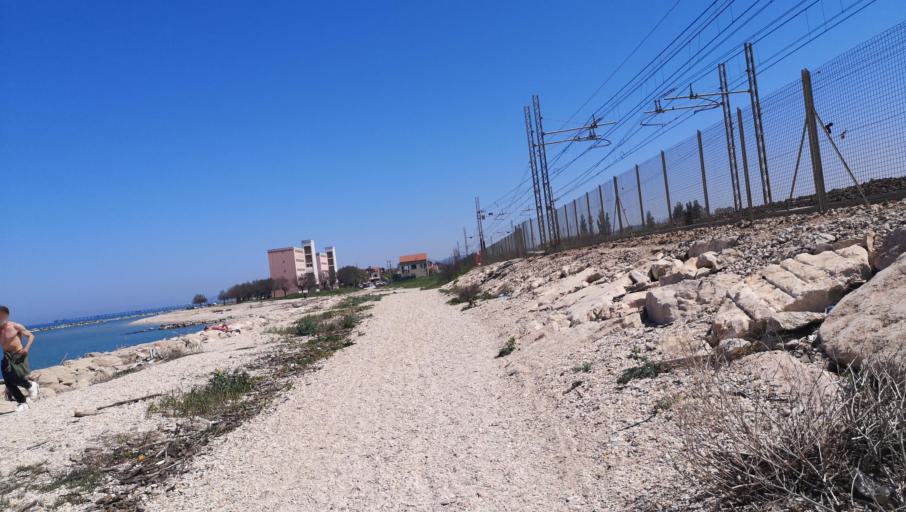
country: IT
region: The Marches
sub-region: Provincia di Ancona
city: Marina di Montemarciano
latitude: 43.6484
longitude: 13.3540
